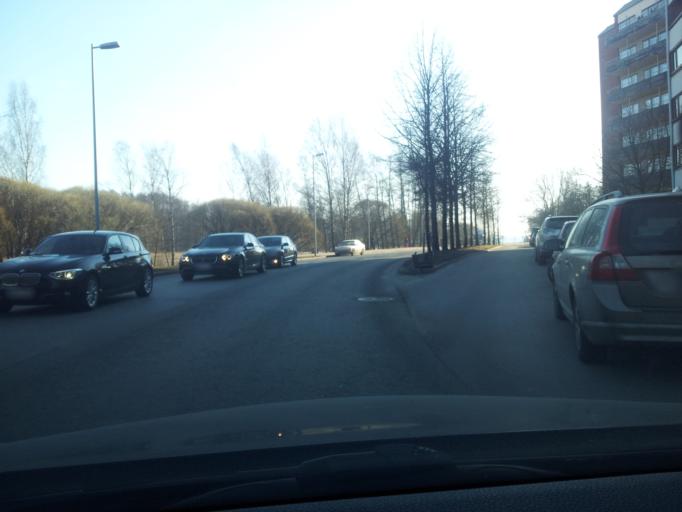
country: FI
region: Uusimaa
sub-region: Helsinki
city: Teekkarikylae
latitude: 60.1954
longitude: 24.8850
